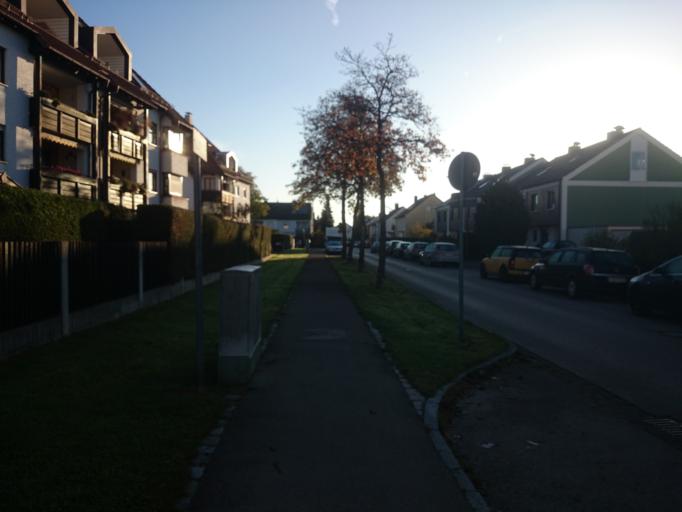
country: DE
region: Bavaria
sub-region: Swabia
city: Konigsbrunn
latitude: 48.2948
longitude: 10.8932
